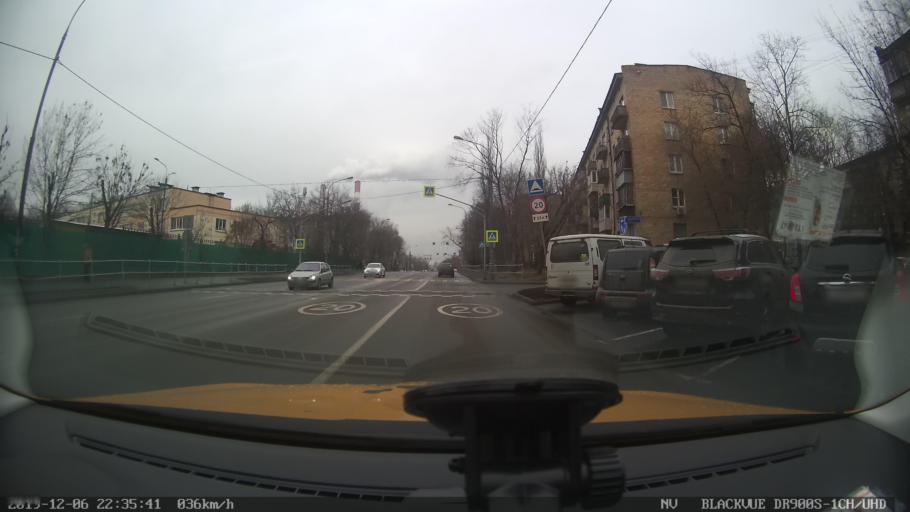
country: RU
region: Moscow
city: Metrogorodok
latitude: 55.8114
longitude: 37.7813
